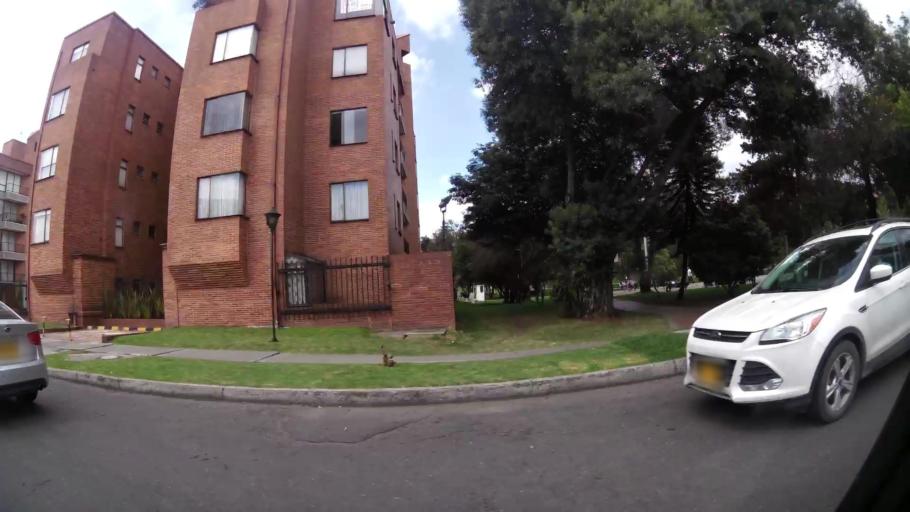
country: CO
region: Bogota D.C.
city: Barrio San Luis
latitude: 4.6998
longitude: -74.0646
